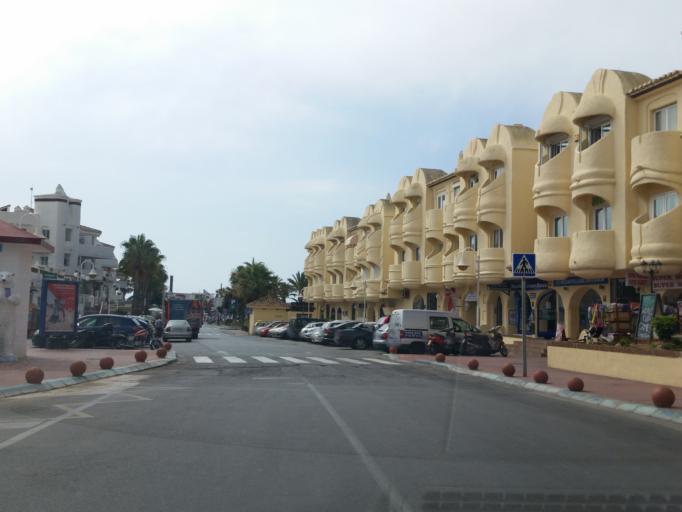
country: ES
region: Andalusia
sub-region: Provincia de Malaga
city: Torremolinos
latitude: 36.5983
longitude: -4.5124
